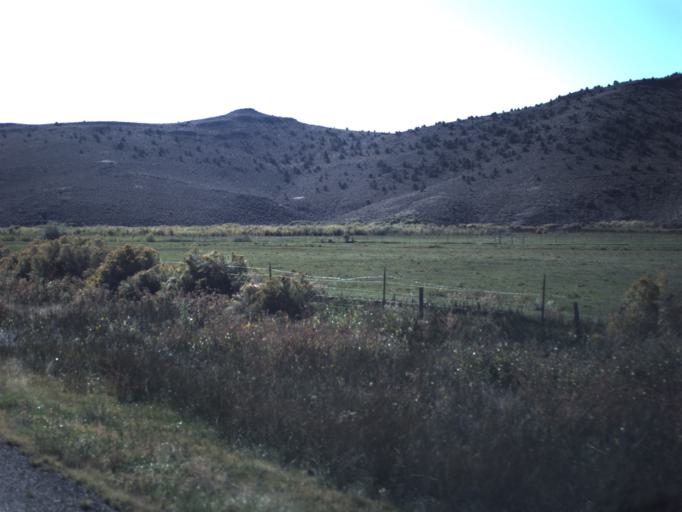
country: US
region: Utah
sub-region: Piute County
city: Junction
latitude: 38.1661
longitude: -112.0362
